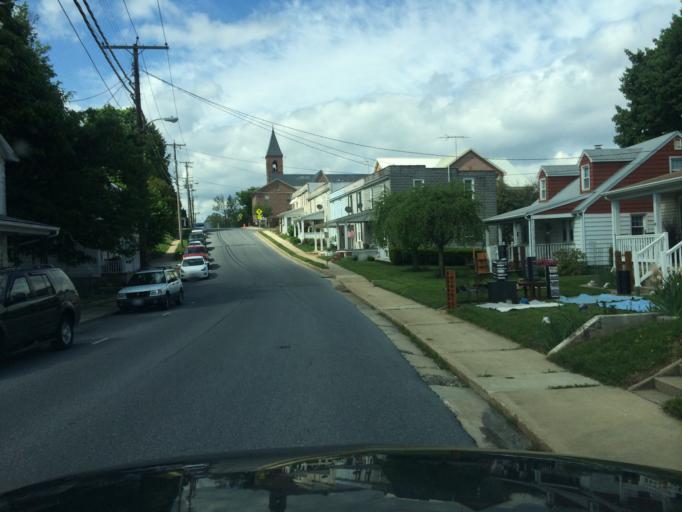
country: US
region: Maryland
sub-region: Carroll County
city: Westminster
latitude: 39.5790
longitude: -76.9958
